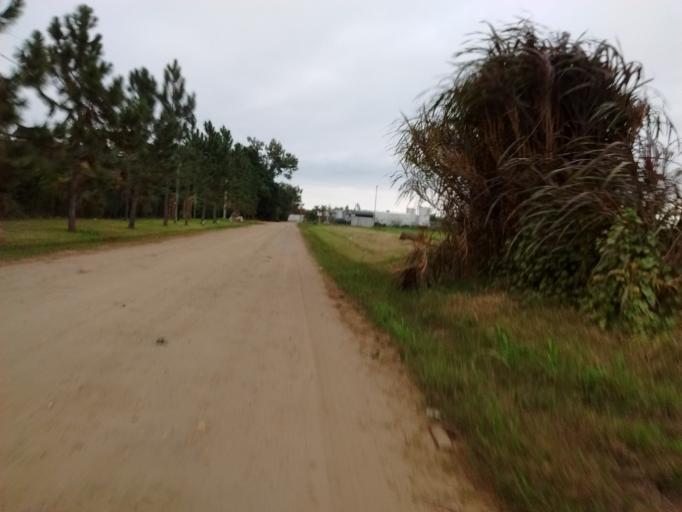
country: AR
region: Santa Fe
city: Funes
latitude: -32.9330
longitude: -60.8286
